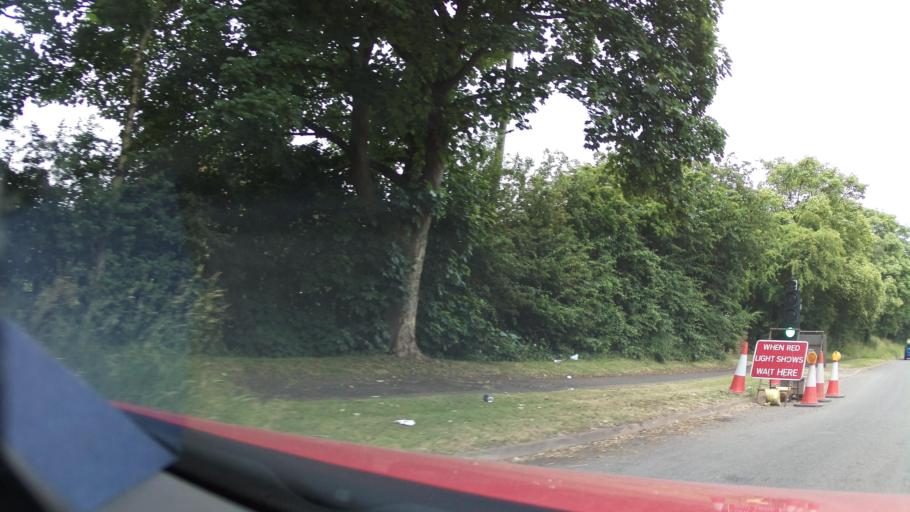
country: GB
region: England
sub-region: Staffordshire
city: Penkridge
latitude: 52.7341
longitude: -2.1114
